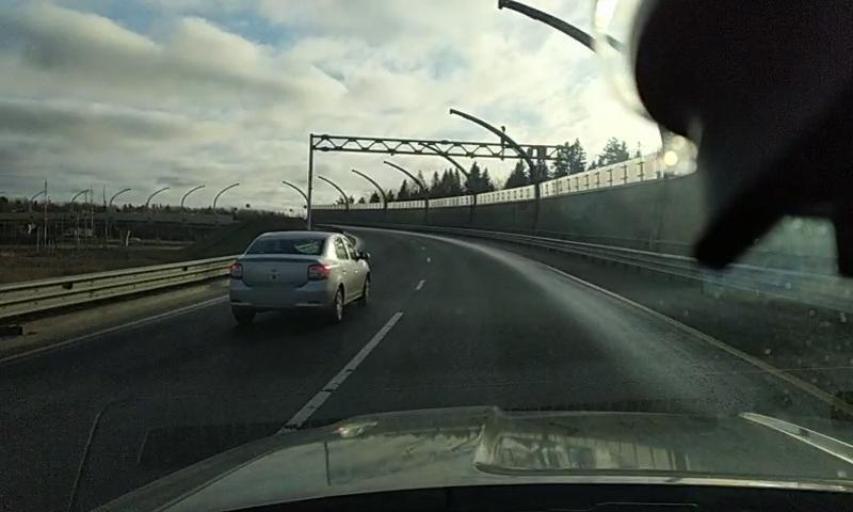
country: RU
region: St.-Petersburg
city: Beloostrov
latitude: 60.1488
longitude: 29.9745
